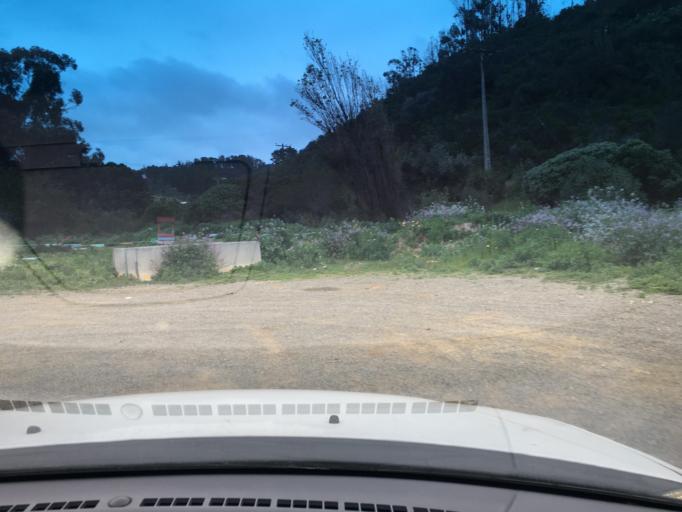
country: CL
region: Valparaiso
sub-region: Provincia de Valparaiso
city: Valparaiso
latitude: -33.1046
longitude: -71.6694
